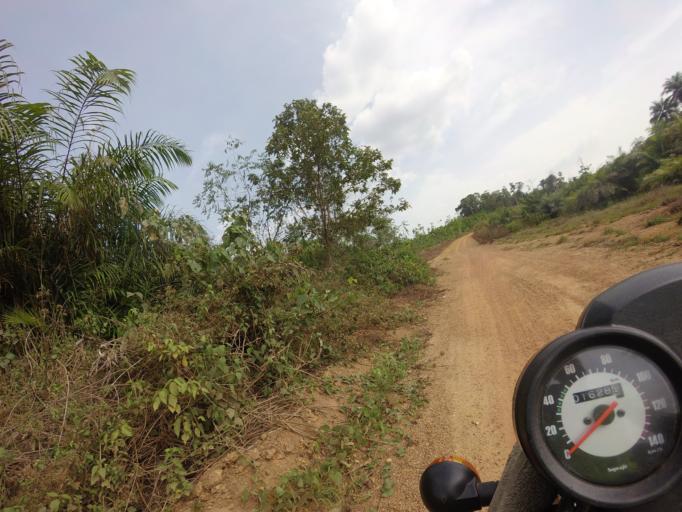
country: SL
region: Southern Province
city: Zimmi
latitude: 7.2368
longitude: -11.1992
